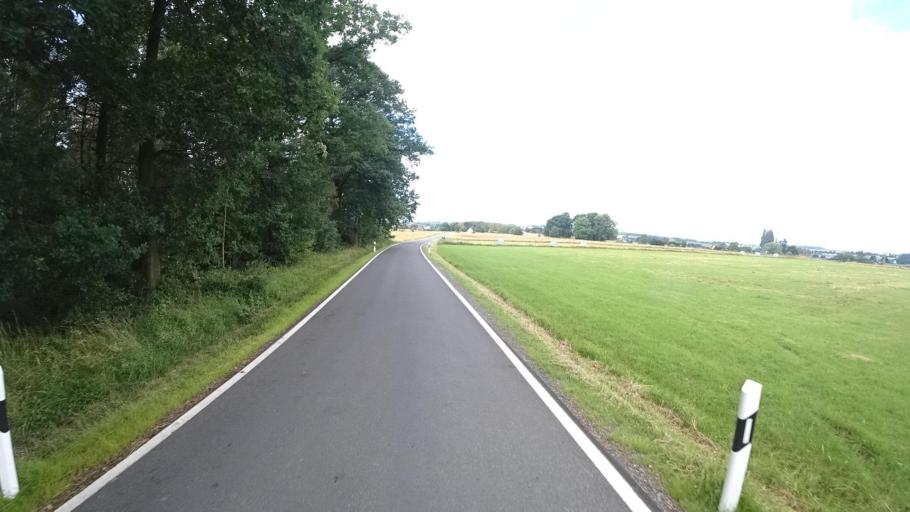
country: DE
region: Rheinland-Pfalz
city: Hirz-Maulsbach
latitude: 50.6894
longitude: 7.4643
